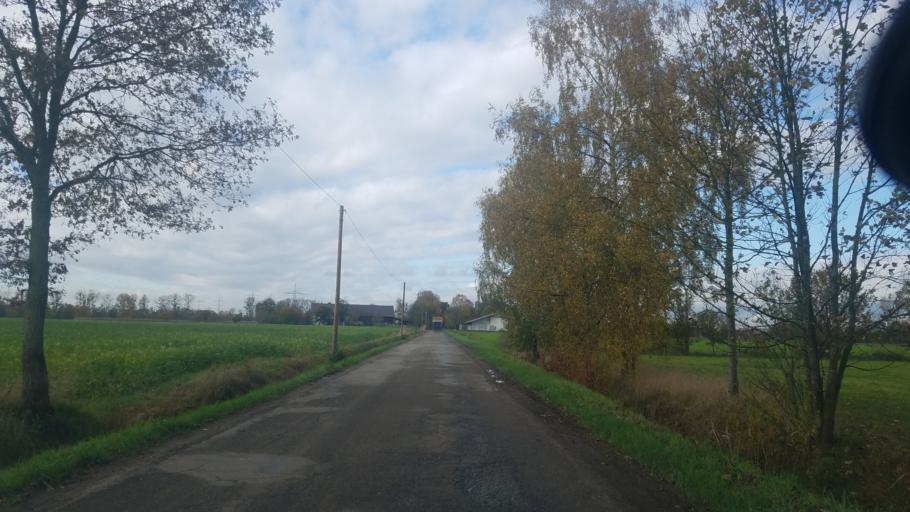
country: DE
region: Baden-Wuerttemberg
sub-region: Freiburg Region
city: Rheinau
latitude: 48.6605
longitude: 7.9979
